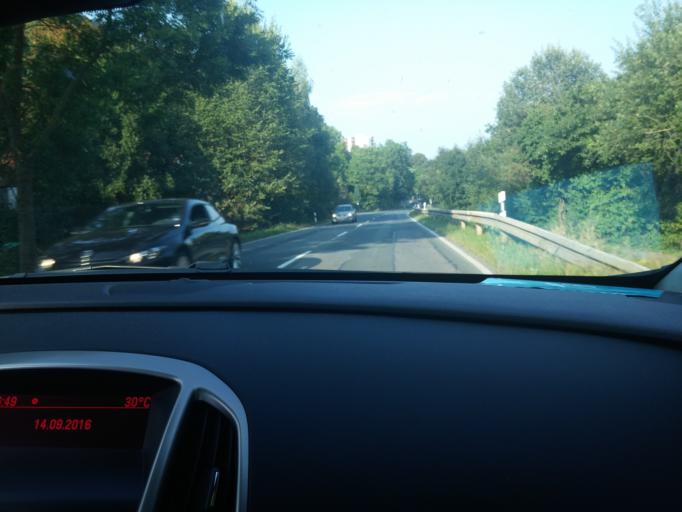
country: DE
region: Bavaria
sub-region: Upper Franconia
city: Coburg
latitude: 50.2619
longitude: 10.9352
